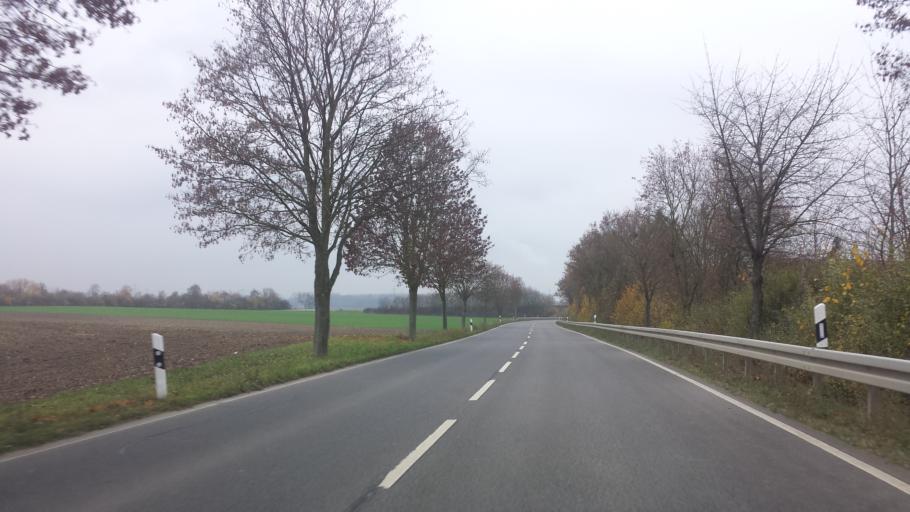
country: DE
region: Rheinland-Pfalz
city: Worms
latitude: 49.6824
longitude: 8.3954
